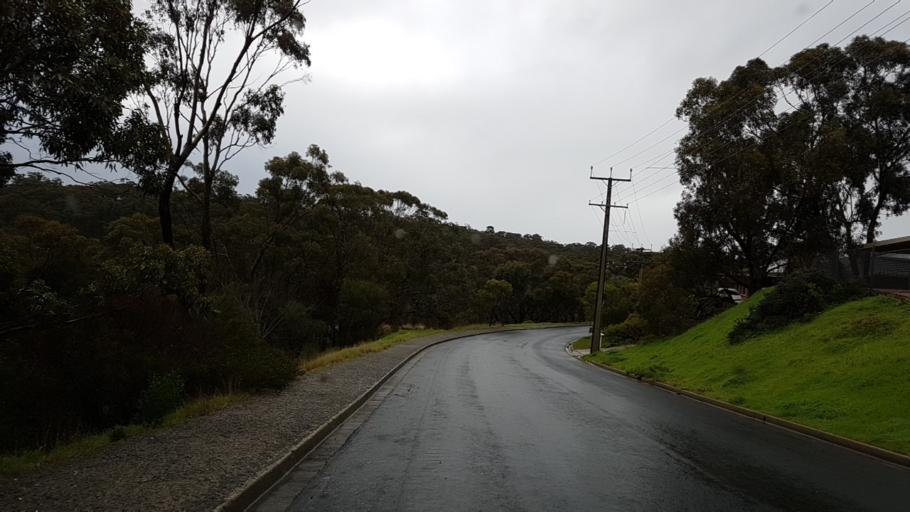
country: AU
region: South Australia
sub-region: Onkaparinga
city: Bedford Park
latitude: -35.0397
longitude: 138.5828
